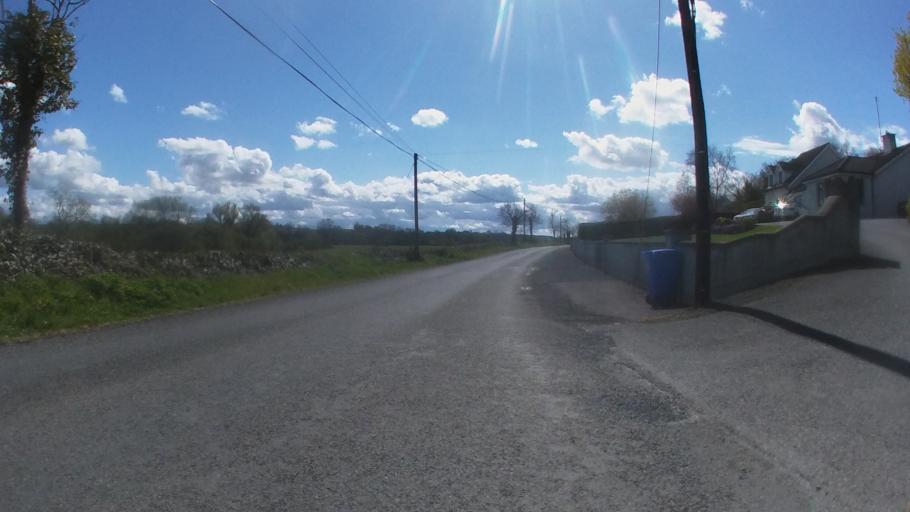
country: IE
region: Leinster
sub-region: Kilkenny
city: Thomastown
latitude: 52.5866
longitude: -7.1855
